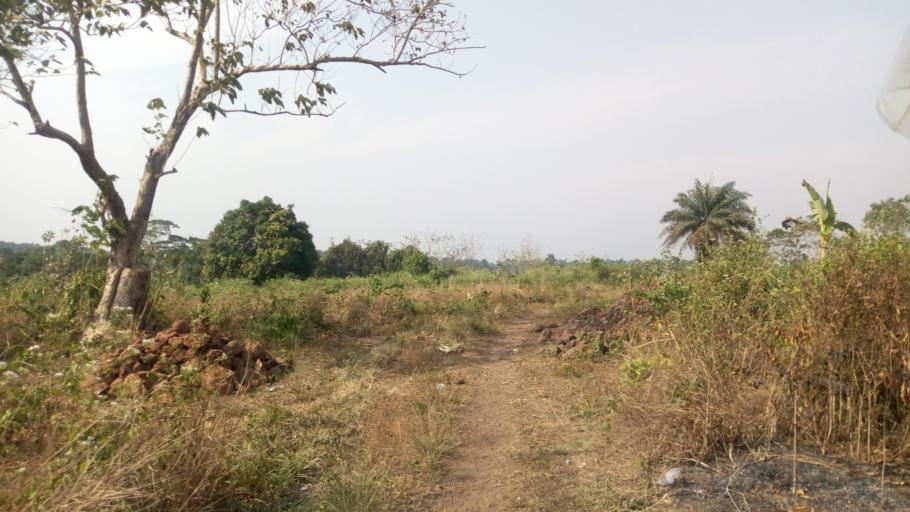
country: SL
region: Southern Province
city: Mogbwemo
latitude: 7.6192
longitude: -12.1810
